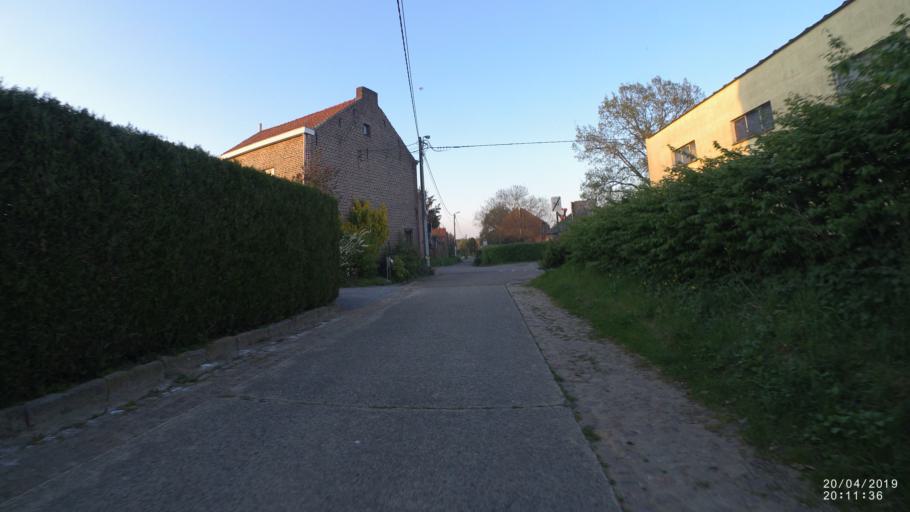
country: BE
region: Flanders
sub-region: Provincie Vlaams-Brabant
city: Lubbeek
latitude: 50.9012
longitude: 4.8078
